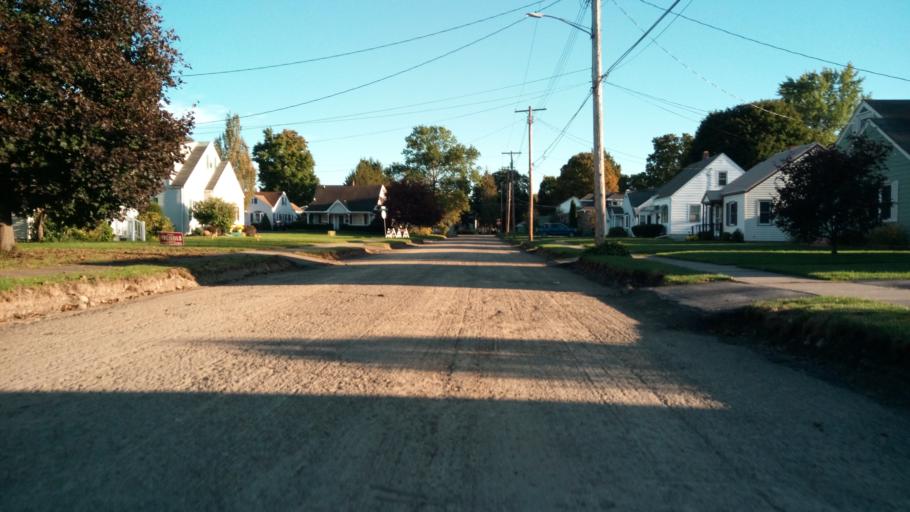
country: US
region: New York
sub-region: Chemung County
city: Elmira
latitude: 42.0777
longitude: -76.8186
